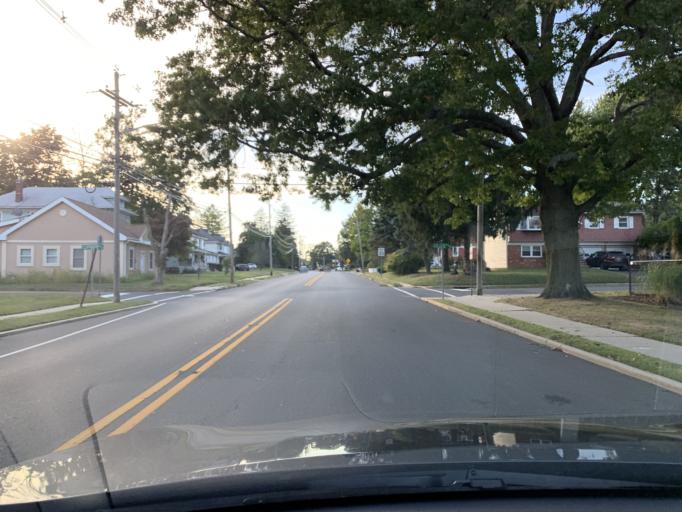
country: US
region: New Jersey
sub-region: Monmouth County
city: Eatontown
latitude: 40.3064
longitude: -74.0512
